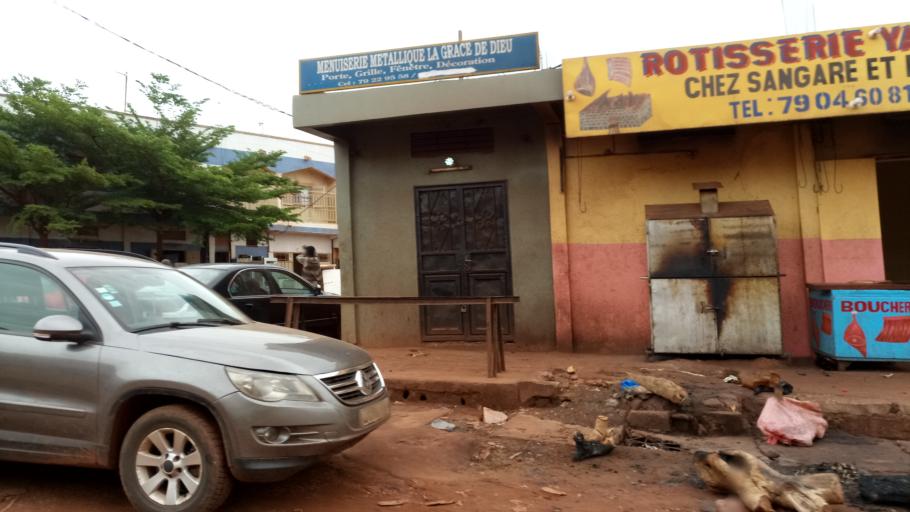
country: ML
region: Bamako
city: Bamako
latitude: 12.5846
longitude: -8.0127
